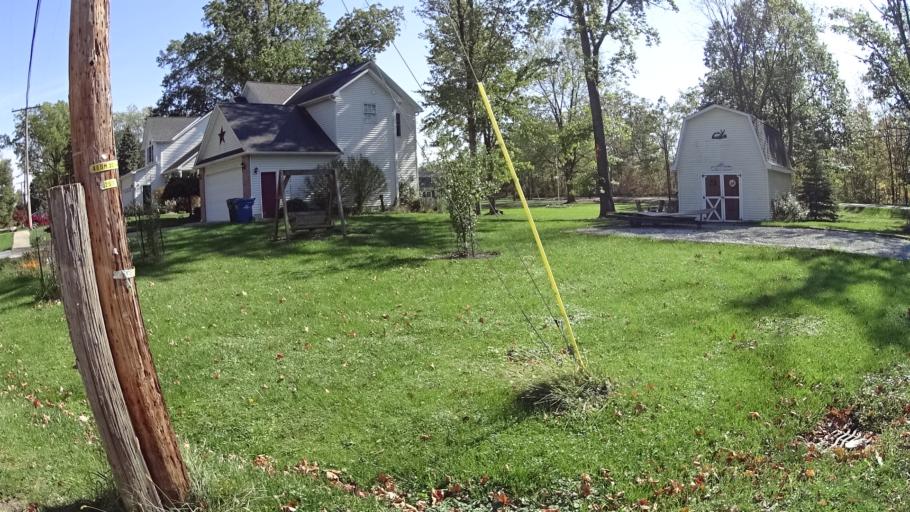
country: US
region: Ohio
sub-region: Lorain County
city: Vermilion
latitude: 41.4158
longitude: -82.3463
